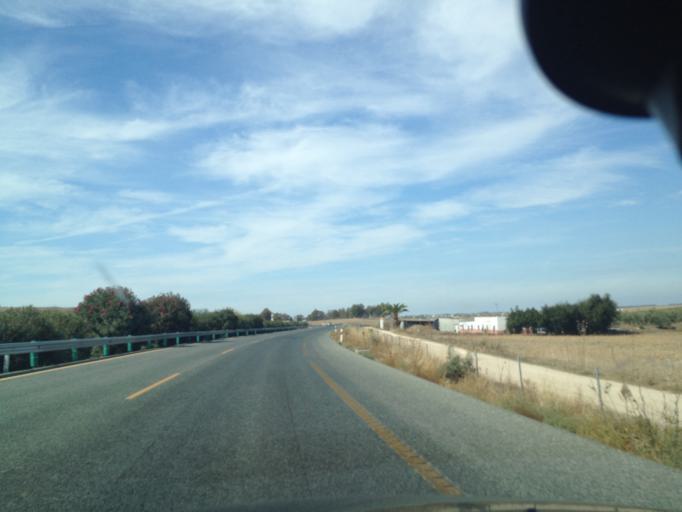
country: ES
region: Andalusia
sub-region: Provincia de Sevilla
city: La Puebla de Cazalla
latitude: 37.2263
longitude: -5.2810
